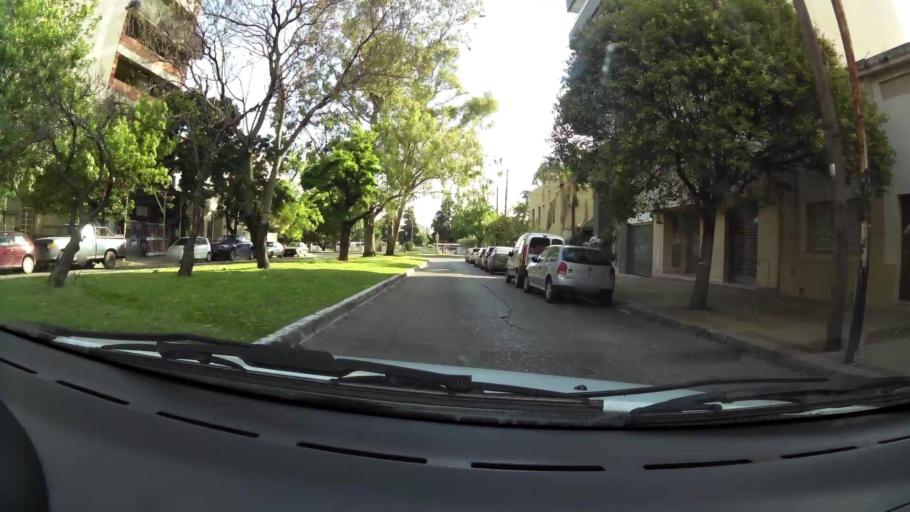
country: AR
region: Buenos Aires
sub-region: Partido de La Plata
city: La Plata
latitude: -34.9047
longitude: -57.9611
